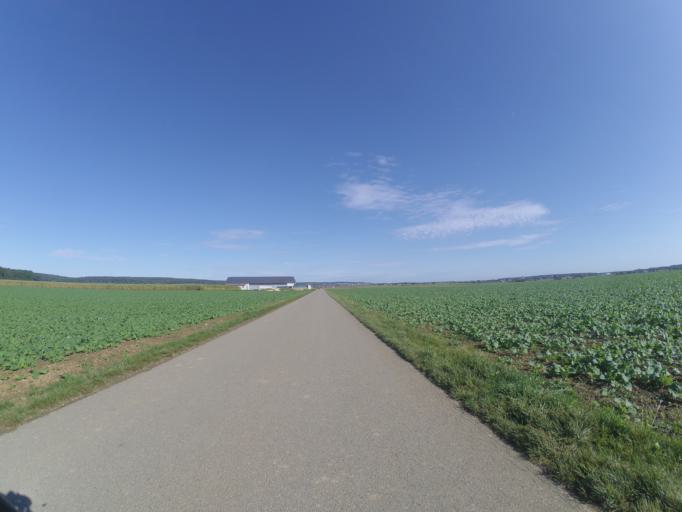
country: DE
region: Baden-Wuerttemberg
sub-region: Tuebingen Region
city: Holzkirch
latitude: 48.5362
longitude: 9.9962
